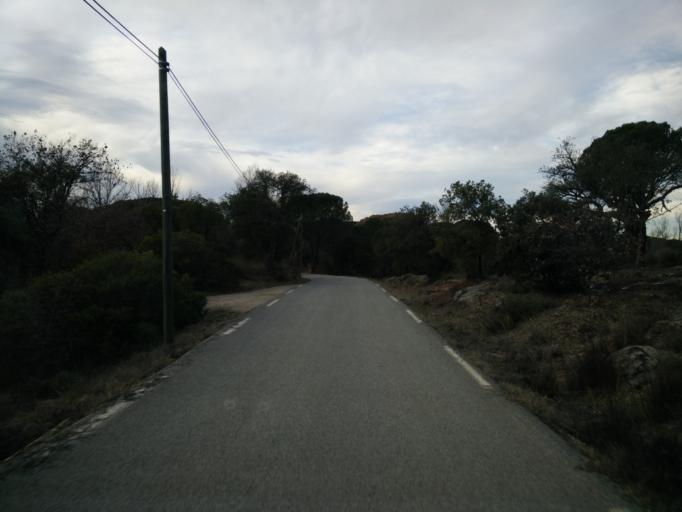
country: FR
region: Provence-Alpes-Cote d'Azur
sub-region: Departement du Var
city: Vidauban
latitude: 43.3931
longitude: 6.4759
